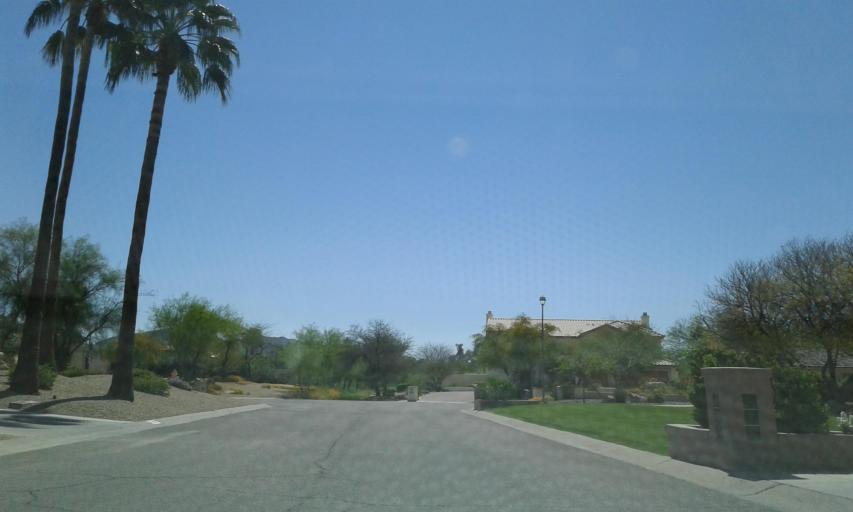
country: US
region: Arizona
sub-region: Maricopa County
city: Paradise Valley
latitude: 33.5855
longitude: -111.9693
